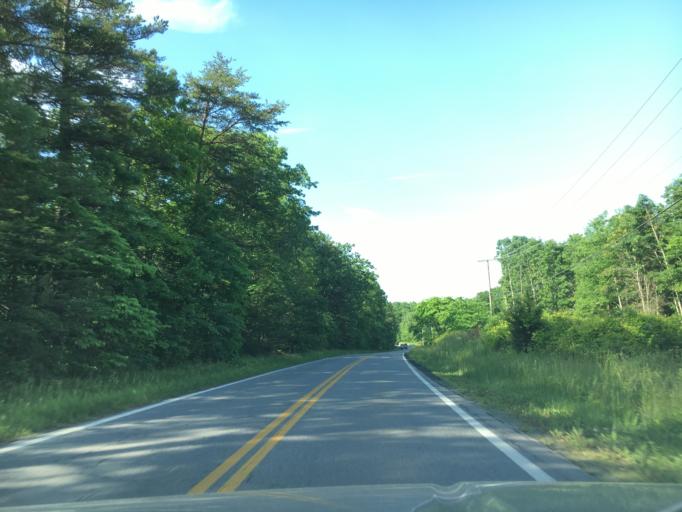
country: US
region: Virginia
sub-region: Campbell County
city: Rustburg
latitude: 37.3215
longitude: -79.1526
